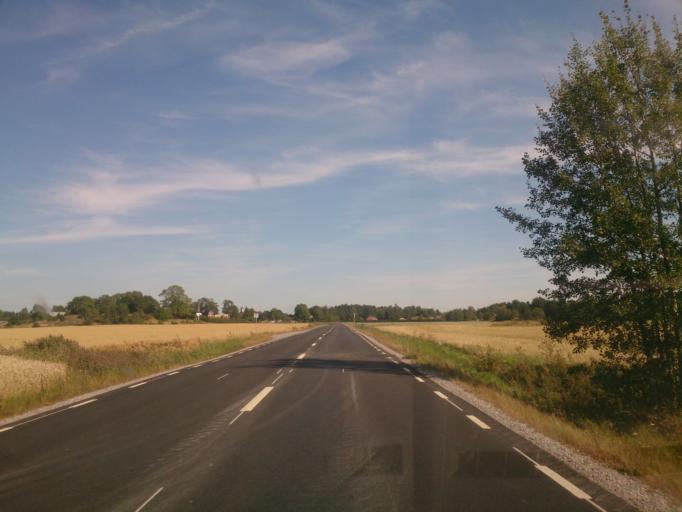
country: SE
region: OEstergoetland
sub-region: Norrkopings Kommun
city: Krokek
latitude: 58.5806
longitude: 16.5396
